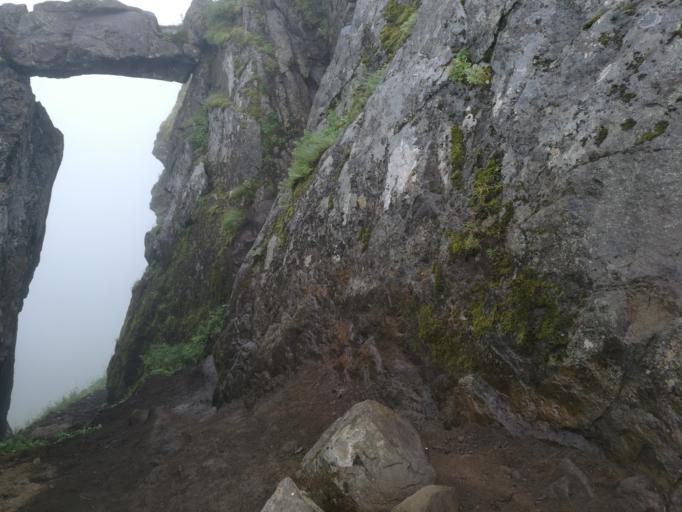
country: NO
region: Nordland
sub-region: Vagan
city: Svolvaer
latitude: 68.2508
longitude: 14.5976
